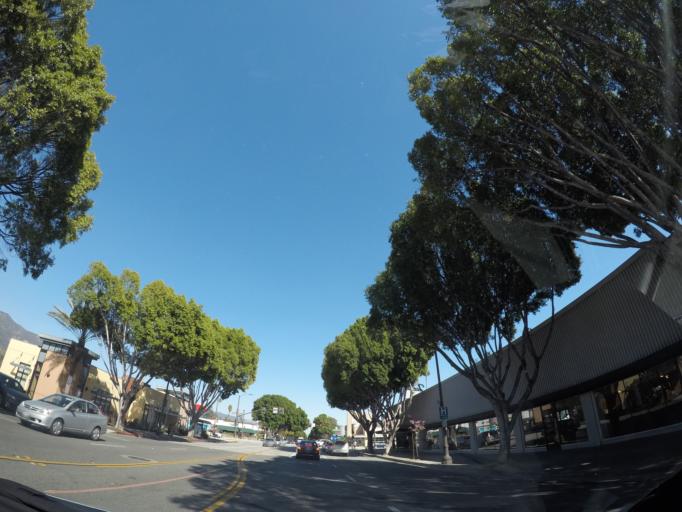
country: US
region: California
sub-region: Los Angeles County
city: East Pasadena
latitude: 34.1461
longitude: -118.1026
